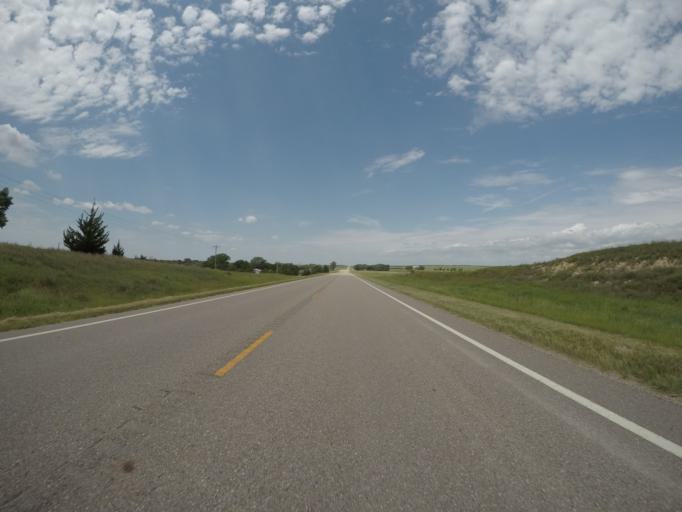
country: US
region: Kansas
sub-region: Graham County
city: Hill City
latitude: 39.3797
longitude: -99.6778
